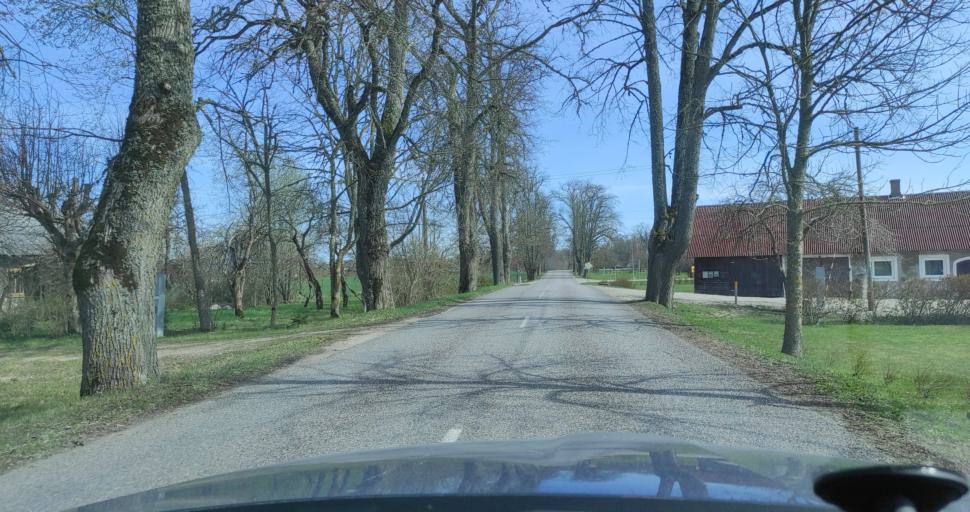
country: LV
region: Talsu Rajons
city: Talsi
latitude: 57.2217
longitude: 22.5101
